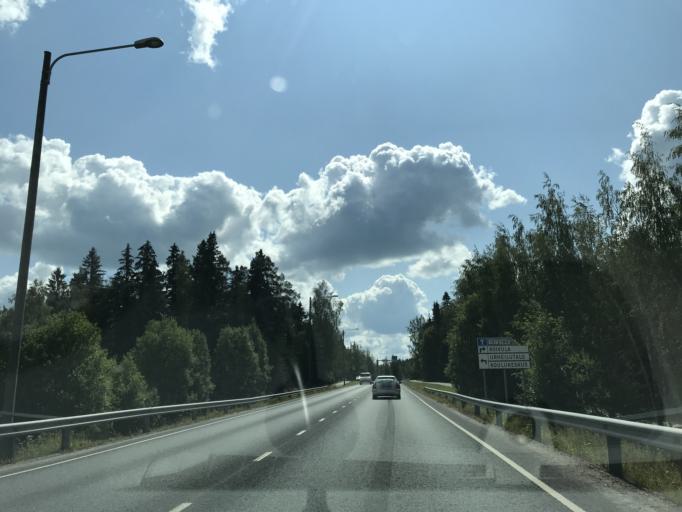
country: FI
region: Paijanne Tavastia
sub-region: Lahti
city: Orimattila
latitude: 60.8215
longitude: 25.7295
